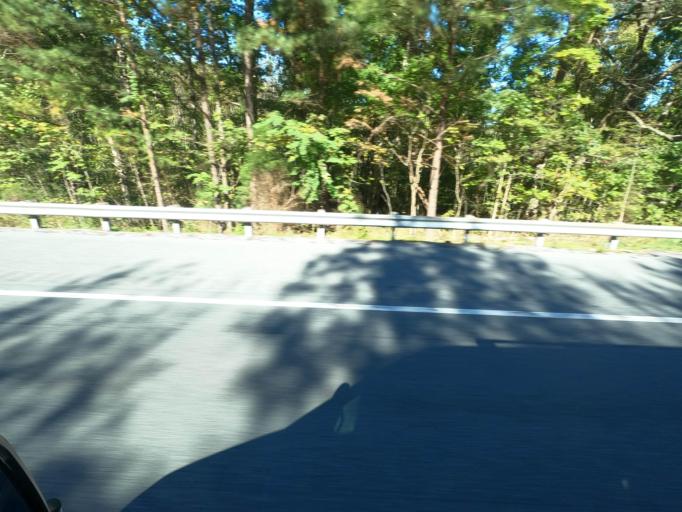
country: US
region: Tennessee
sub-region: Williamson County
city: Fairview
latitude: 36.0434
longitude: -87.1477
